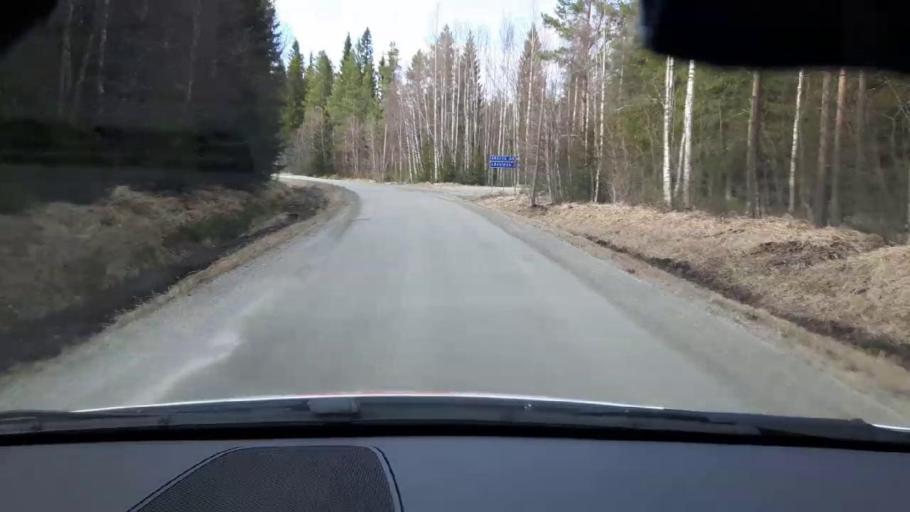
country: SE
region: Jaemtland
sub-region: Bergs Kommun
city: Hoverberg
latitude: 62.6790
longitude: 14.7478
